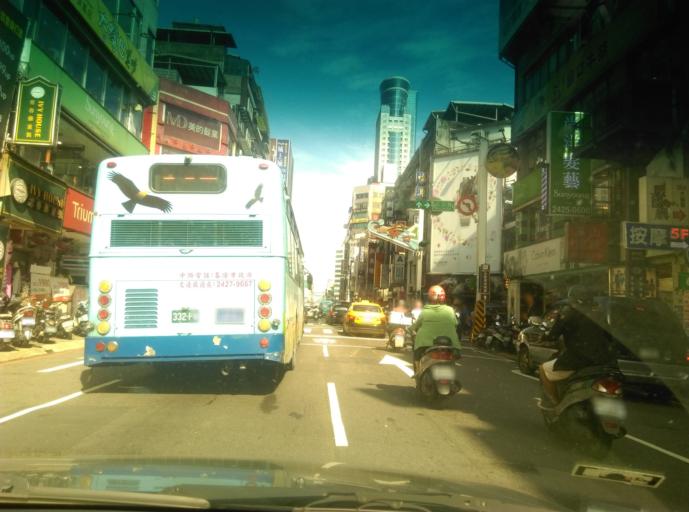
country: TW
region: Taiwan
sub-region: Keelung
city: Keelung
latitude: 25.1284
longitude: 121.7426
